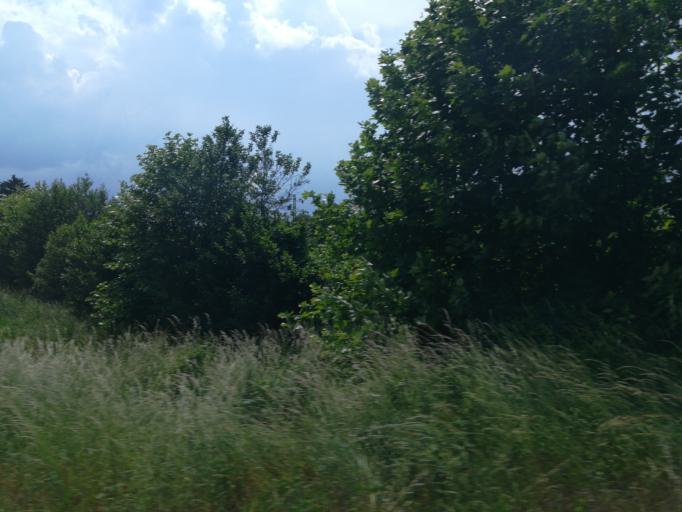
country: IT
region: Veneto
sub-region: Provincia di Vicenza
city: Monticello Conte Otto
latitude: 45.6159
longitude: 11.5671
